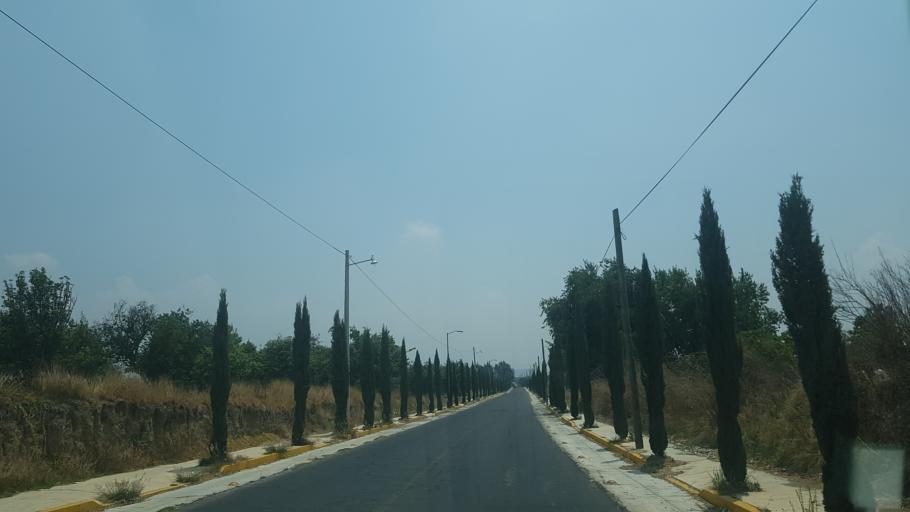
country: MX
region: Puebla
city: San Andres Calpan
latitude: 19.1029
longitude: -98.4464
